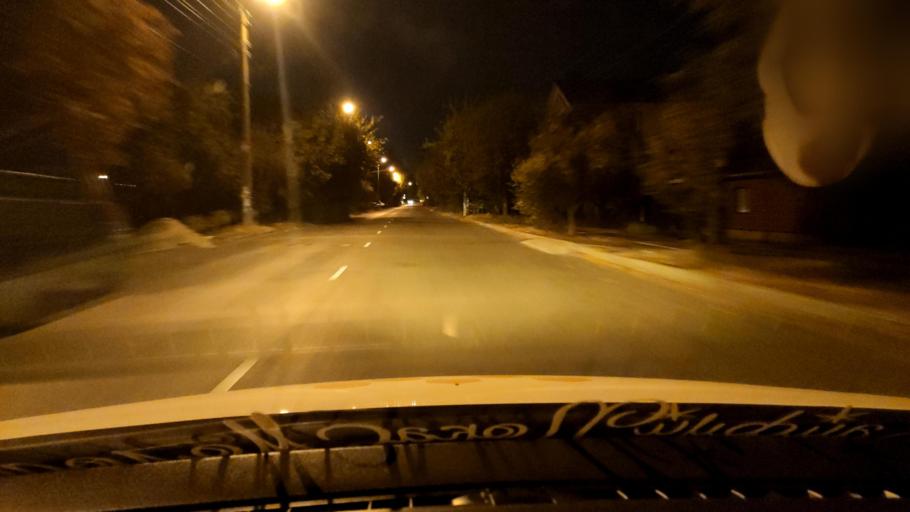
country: RU
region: Voronezj
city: Voronezh
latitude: 51.6424
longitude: 39.1710
